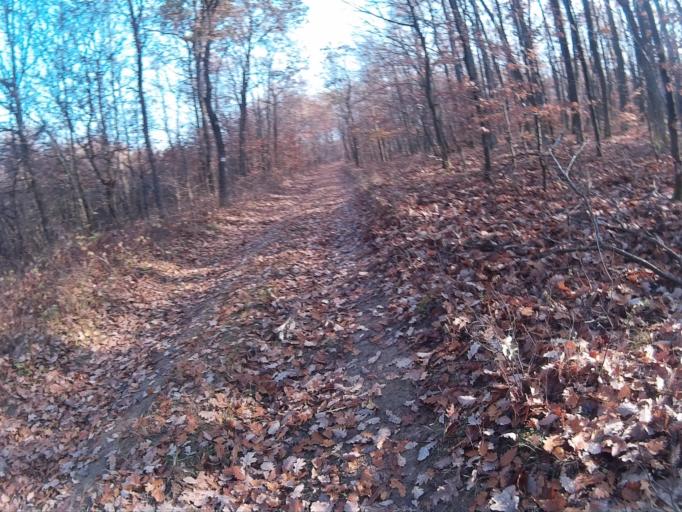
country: HU
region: Heves
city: Felsotarkany
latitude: 48.0049
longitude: 20.3997
